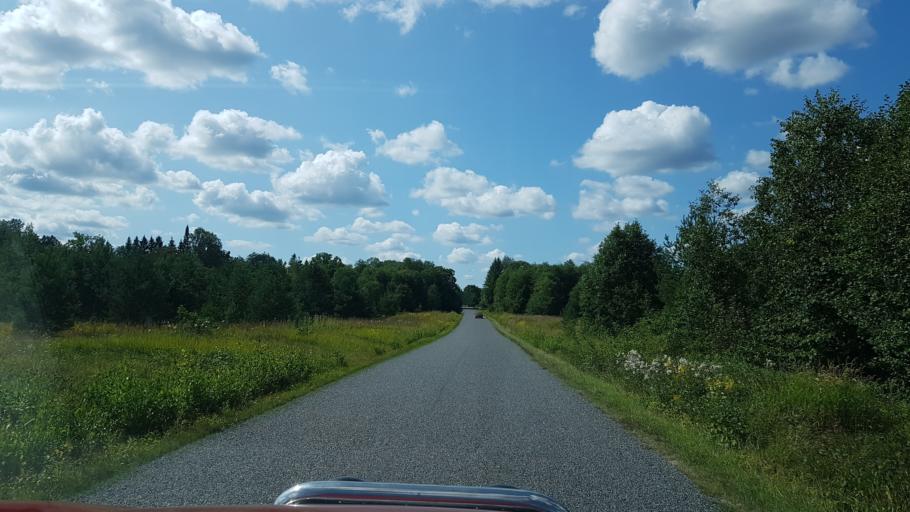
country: EE
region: Vorumaa
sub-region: Voru linn
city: Voru
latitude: 57.7283
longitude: 27.2257
